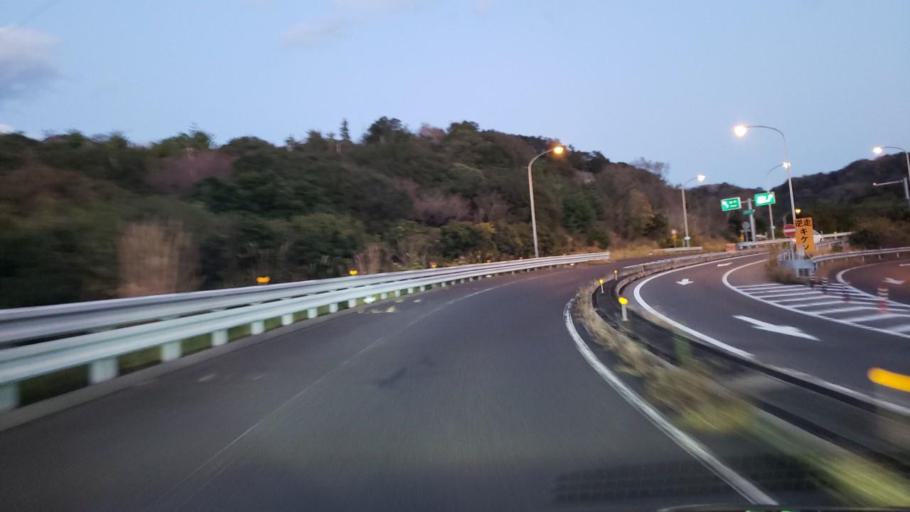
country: JP
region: Hyogo
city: Fukura
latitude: 34.2607
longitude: 134.6823
